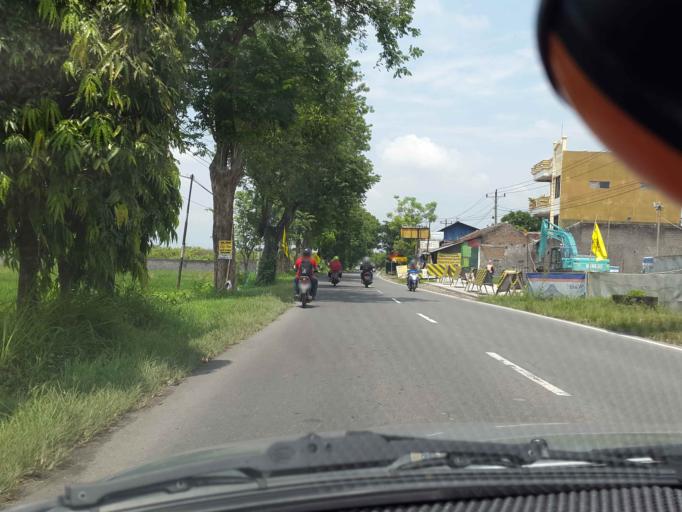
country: ID
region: Central Java
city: Surakarta
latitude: -7.5359
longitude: 110.7982
